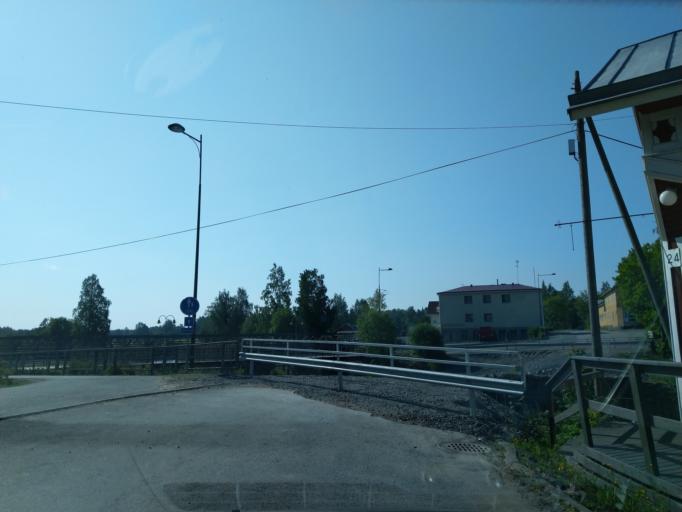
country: FI
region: Satakunta
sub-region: Pori
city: Pomarkku
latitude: 61.6968
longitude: 22.0117
